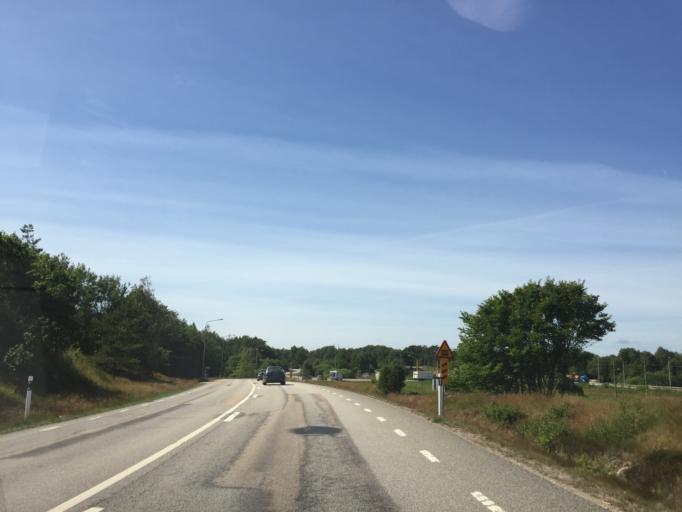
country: SE
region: Vaestra Goetaland
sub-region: Lysekils Kommun
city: Lysekil
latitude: 58.3047
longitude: 11.4802
